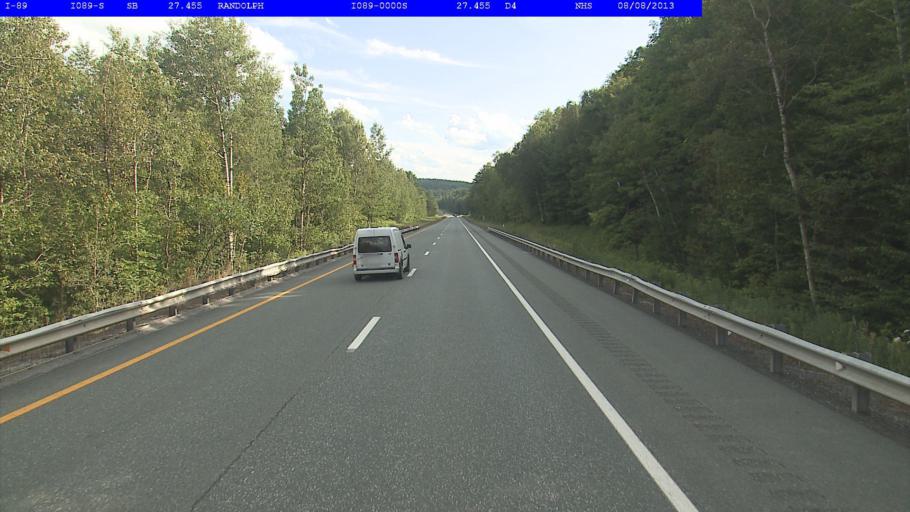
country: US
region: Vermont
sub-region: Orange County
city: Randolph
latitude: 43.8966
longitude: -72.6165
